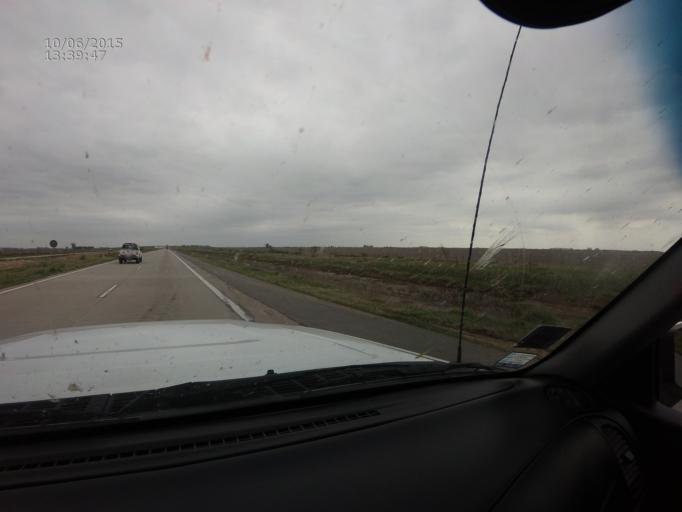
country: AR
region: Cordoba
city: Leones
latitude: -32.5988
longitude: -62.4641
